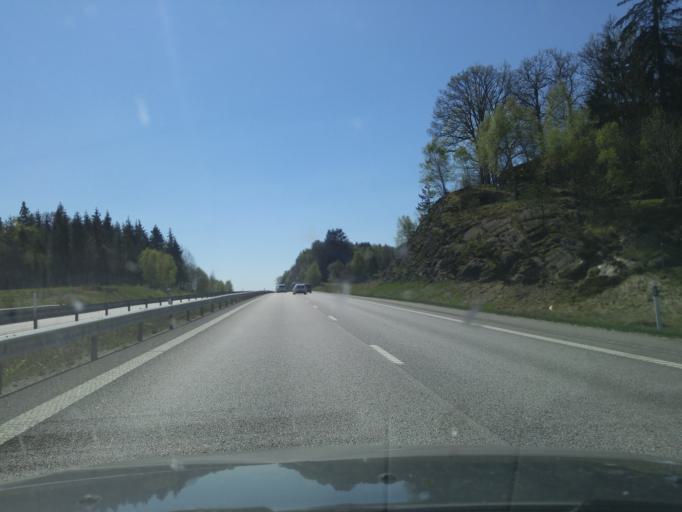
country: SE
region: Vaestra Goetaland
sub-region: Uddevalla Kommun
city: Ljungskile
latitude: 58.2601
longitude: 11.8984
